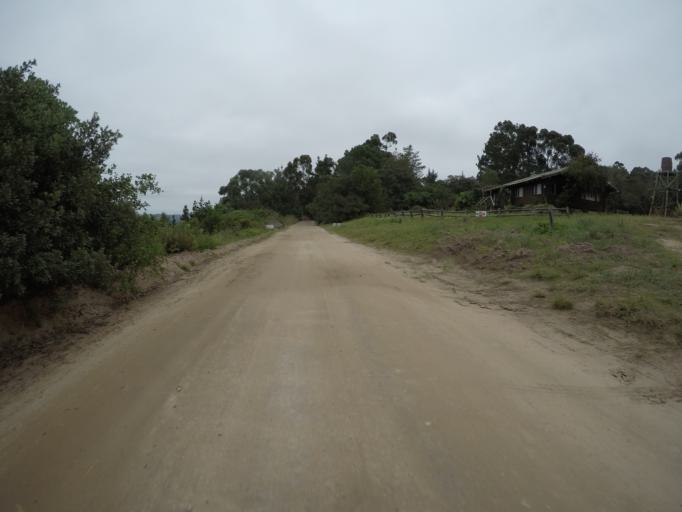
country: ZA
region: Western Cape
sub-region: Eden District Municipality
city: Knysna
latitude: -34.0082
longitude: 22.7994
